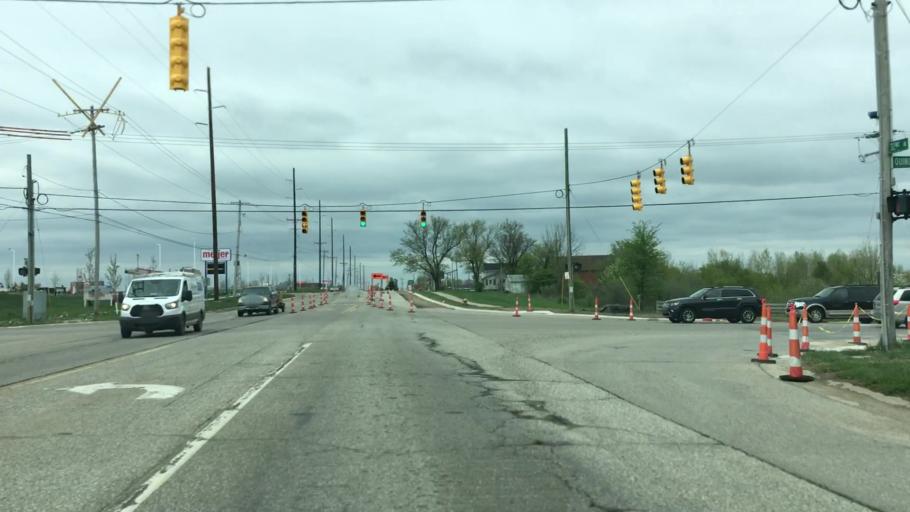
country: US
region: Michigan
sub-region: Ottawa County
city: Hudsonville
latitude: 42.8401
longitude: -85.8618
